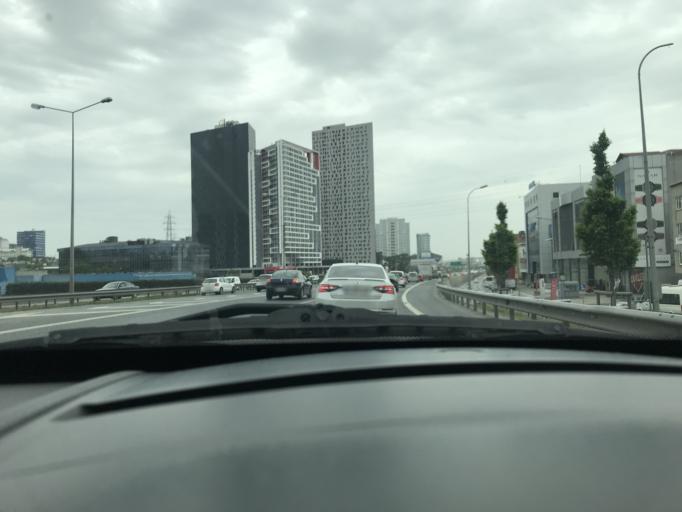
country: TR
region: Istanbul
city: Mahmutbey
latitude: 41.0588
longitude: 28.8103
